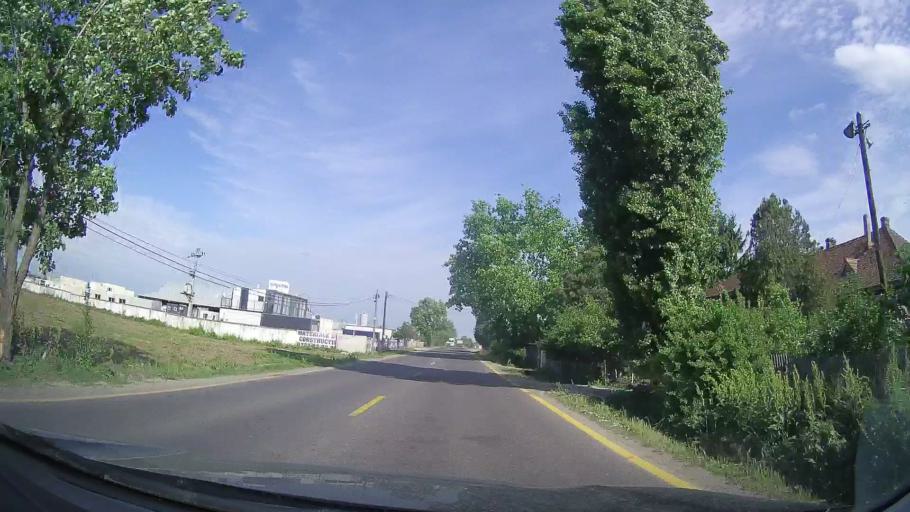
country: RO
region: Ilfov
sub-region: Comuna Magurele
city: Varteju
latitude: 44.3685
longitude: 26.0146
